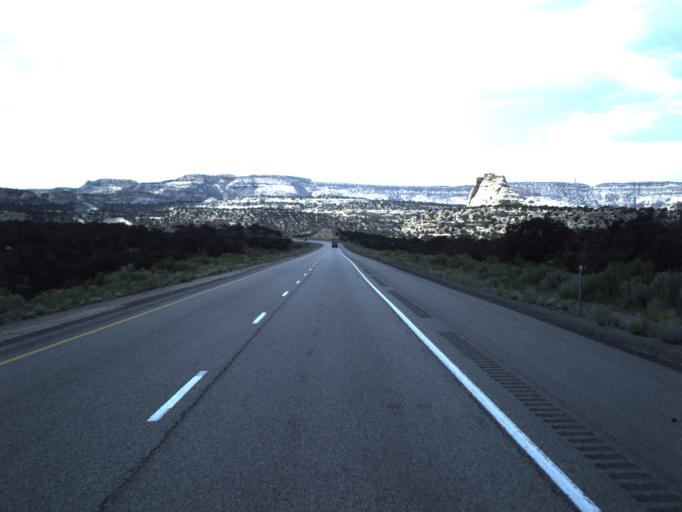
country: US
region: Utah
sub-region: Emery County
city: Ferron
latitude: 38.8642
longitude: -110.8552
